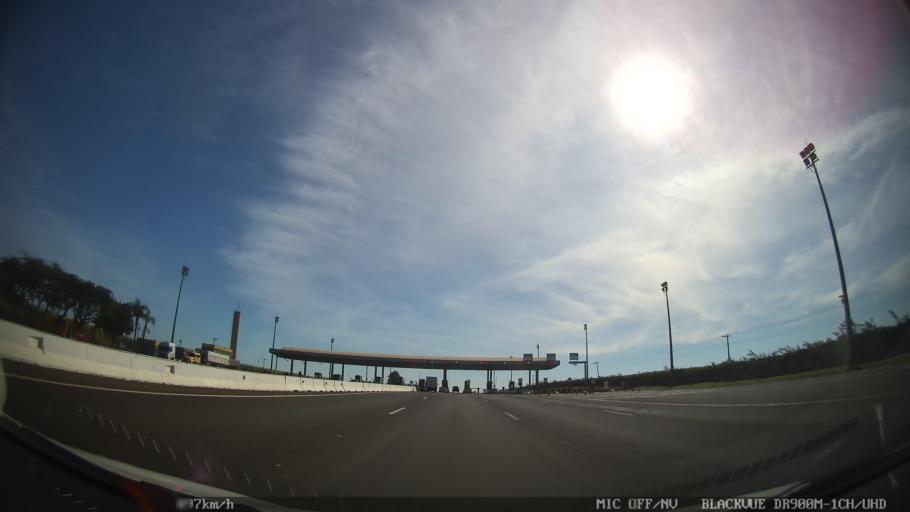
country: BR
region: Sao Paulo
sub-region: Leme
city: Leme
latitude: -22.2508
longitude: -47.3899
